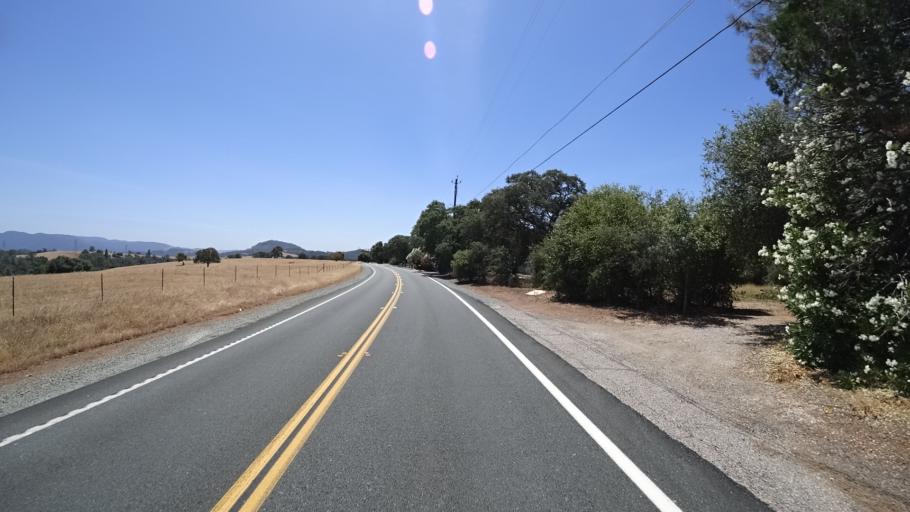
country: US
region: California
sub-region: Amador County
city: Jackson
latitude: 38.2921
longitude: -120.7129
